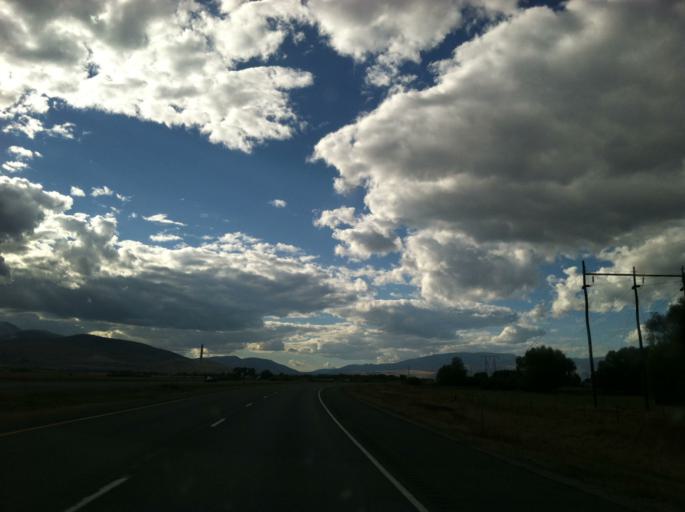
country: US
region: Montana
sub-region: Deer Lodge County
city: Warm Springs
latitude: 46.0966
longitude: -112.8258
